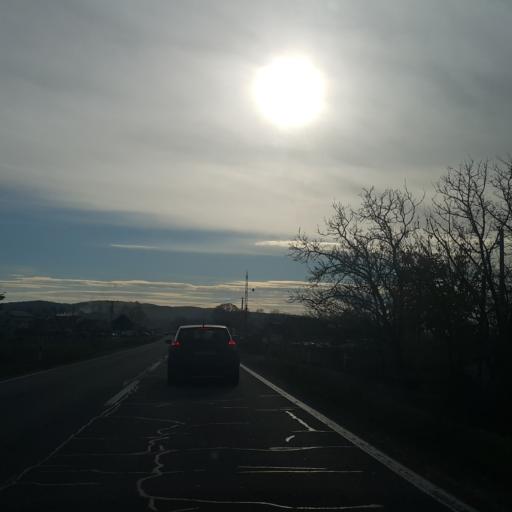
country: RS
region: Central Serbia
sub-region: Belgrade
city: Lazarevac
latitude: 44.3960
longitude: 20.2434
